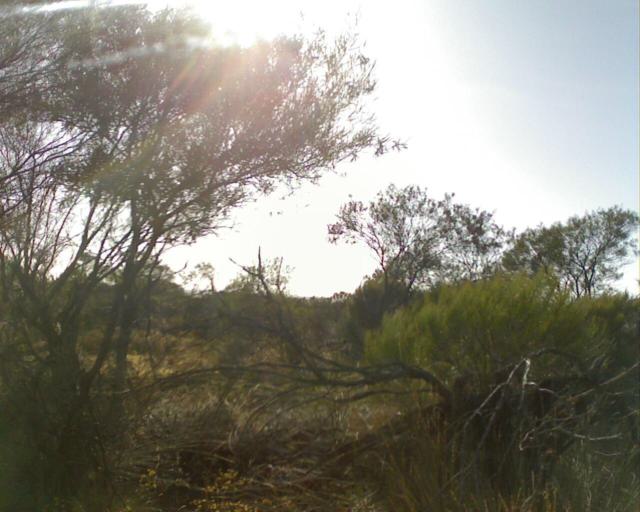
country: AU
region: Western Australia
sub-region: Wongan-Ballidu
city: Wongan Hills
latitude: -30.2894
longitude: 116.9660
